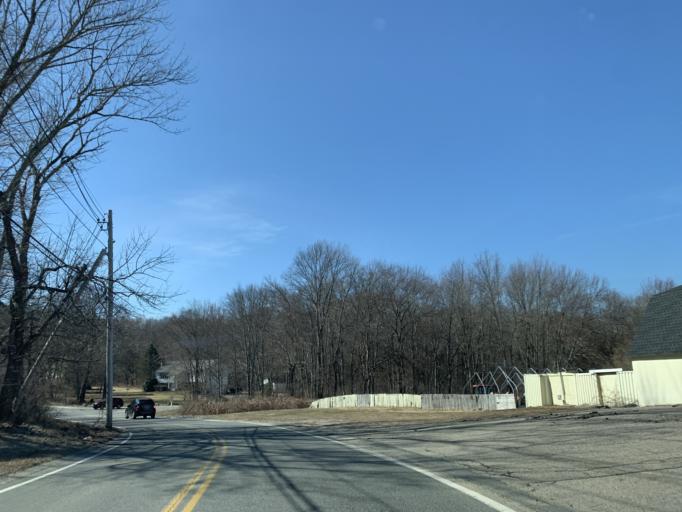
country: US
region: Massachusetts
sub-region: Norfolk County
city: Sharon
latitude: 42.1486
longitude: -71.1872
